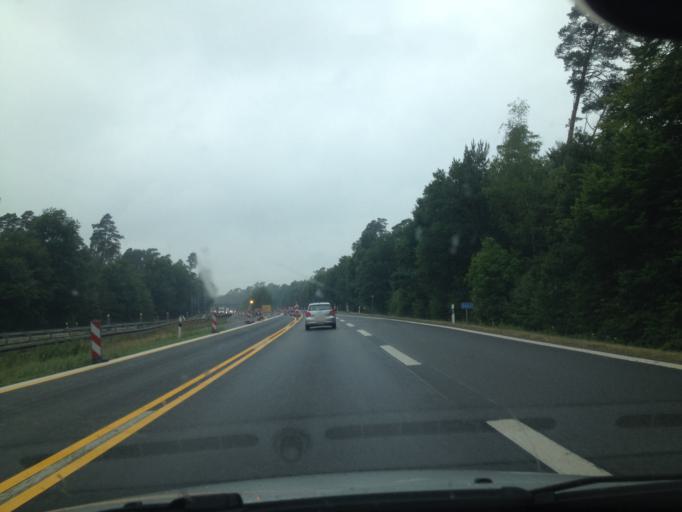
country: DE
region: Bavaria
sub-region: Regierungsbezirk Unterfranken
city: Kahl am Main
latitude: 50.1005
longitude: 9.0261
